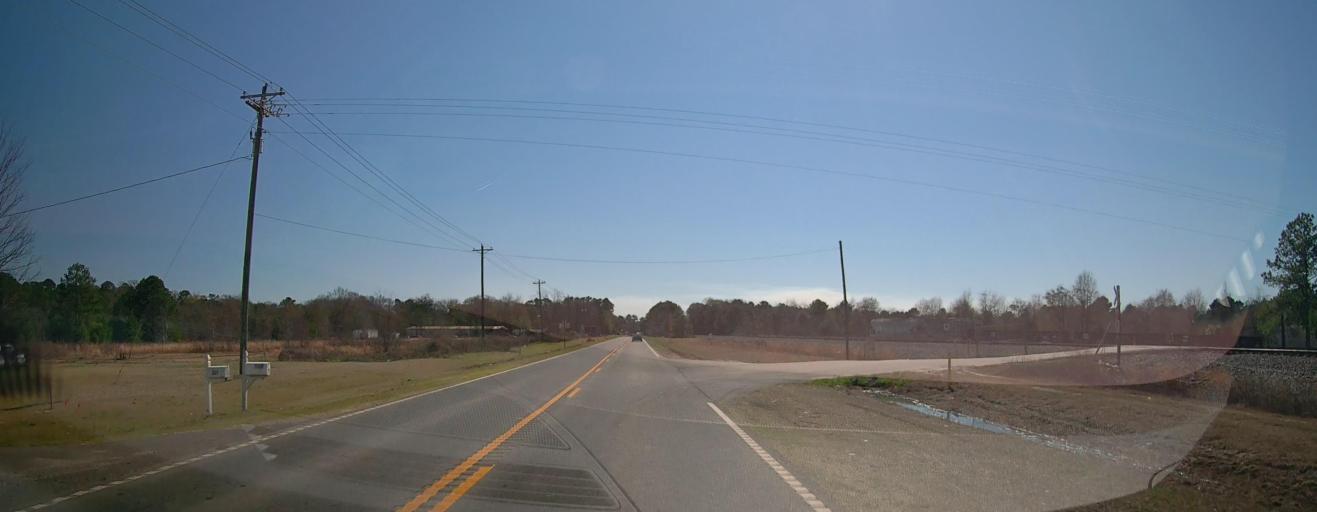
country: US
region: Georgia
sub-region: Houston County
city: Perry
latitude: 32.4645
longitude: -83.6176
